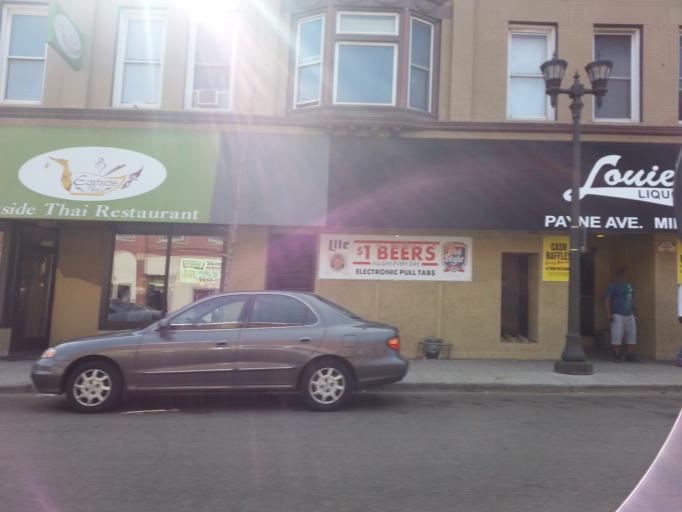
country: US
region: Minnesota
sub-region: Ramsey County
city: Saint Paul
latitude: 44.9679
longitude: -93.0736
